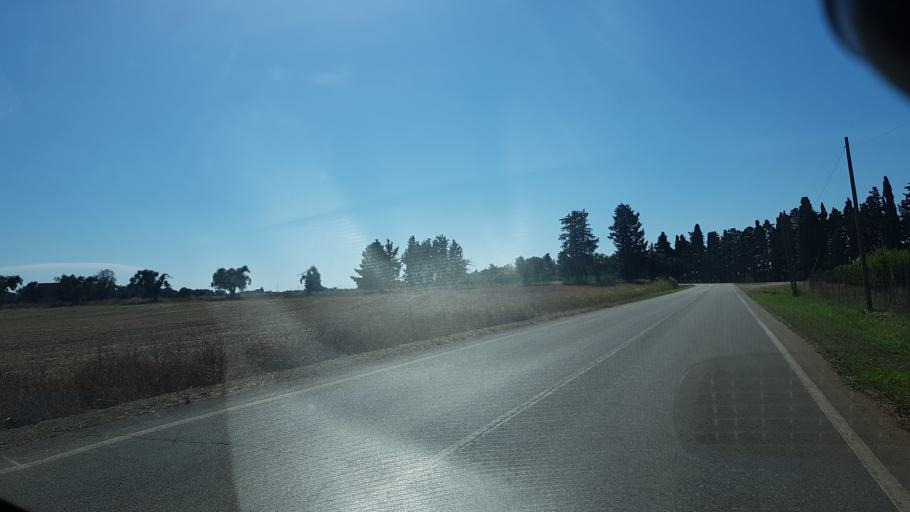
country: IT
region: Apulia
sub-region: Provincia di Brindisi
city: Mesagne
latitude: 40.5572
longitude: 17.8486
